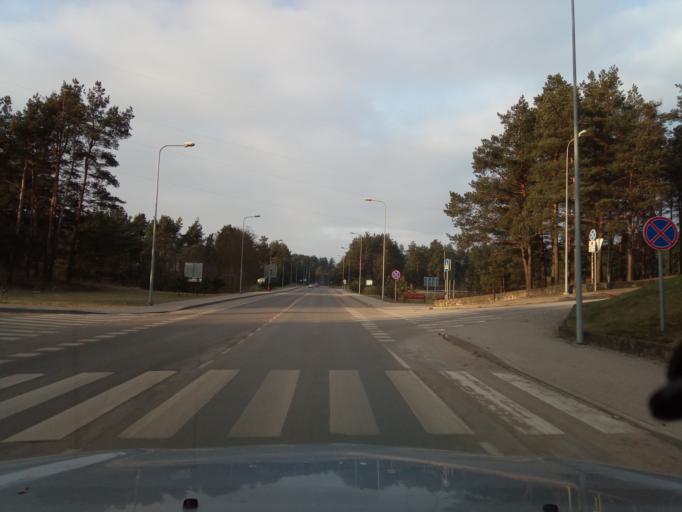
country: LT
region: Alytaus apskritis
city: Varena
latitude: 54.2191
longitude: 24.5606
